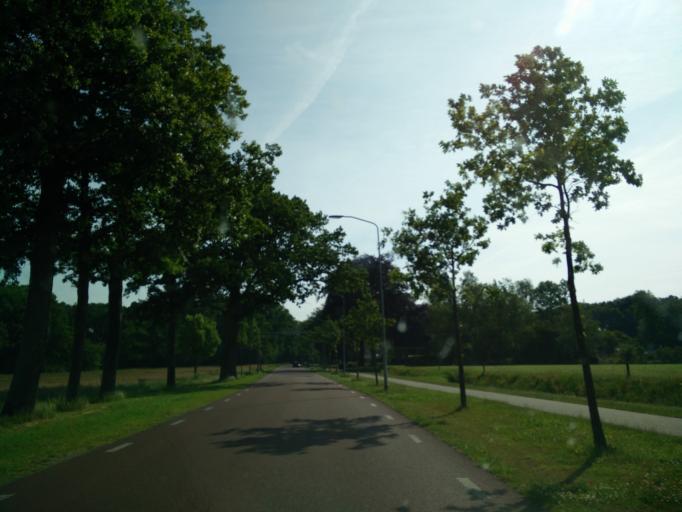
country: NL
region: Drenthe
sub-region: Gemeente Assen
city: Assen
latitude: 52.9895
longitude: 6.6119
